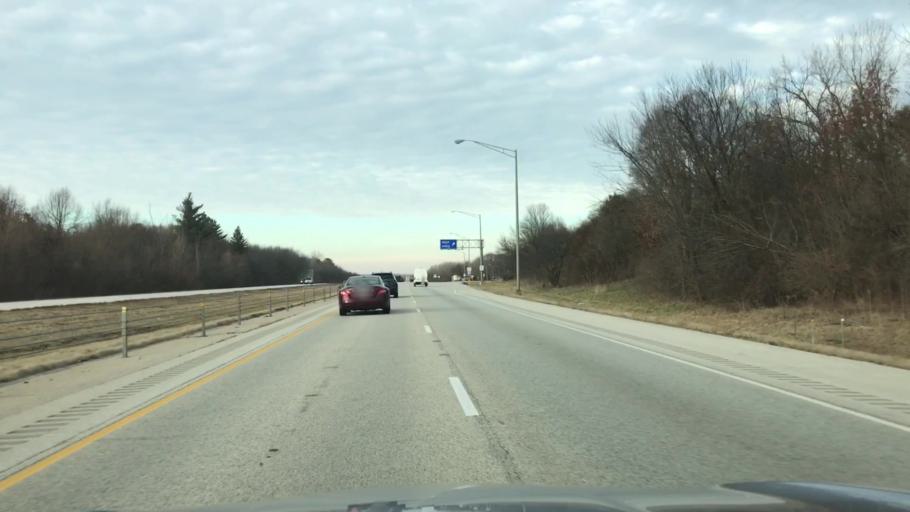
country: US
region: Illinois
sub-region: Sangamon County
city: Sherman
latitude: 39.8604
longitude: -89.5952
